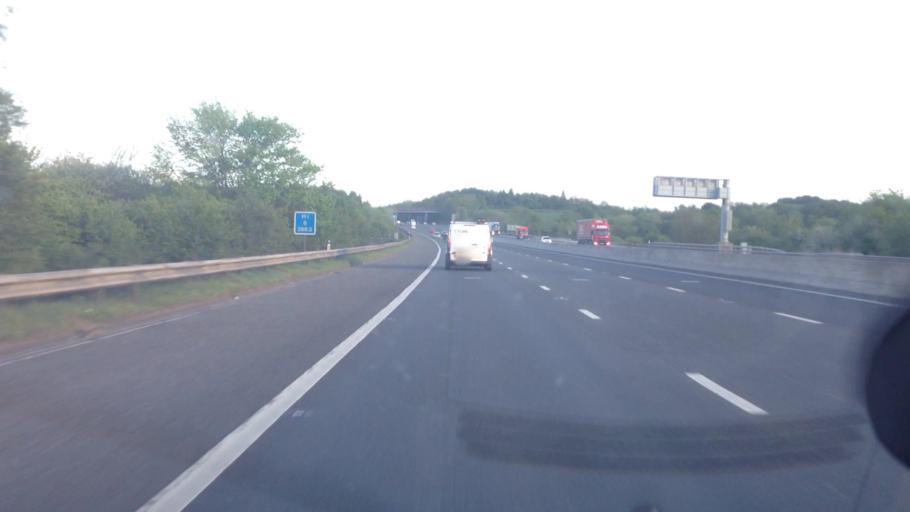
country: GB
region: England
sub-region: Sheffield
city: Chapletown
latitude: 53.4844
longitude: -1.4667
